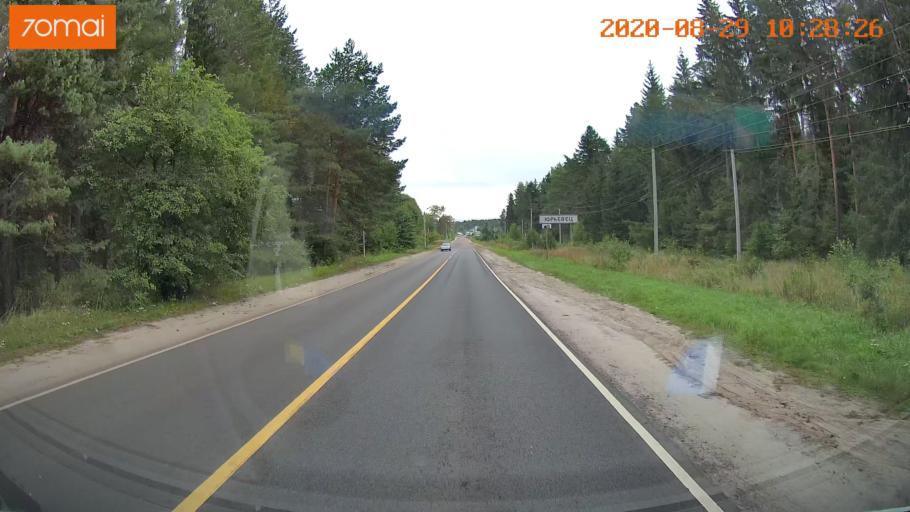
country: RU
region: Ivanovo
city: Yur'yevets
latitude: 57.3114
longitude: 43.0920
